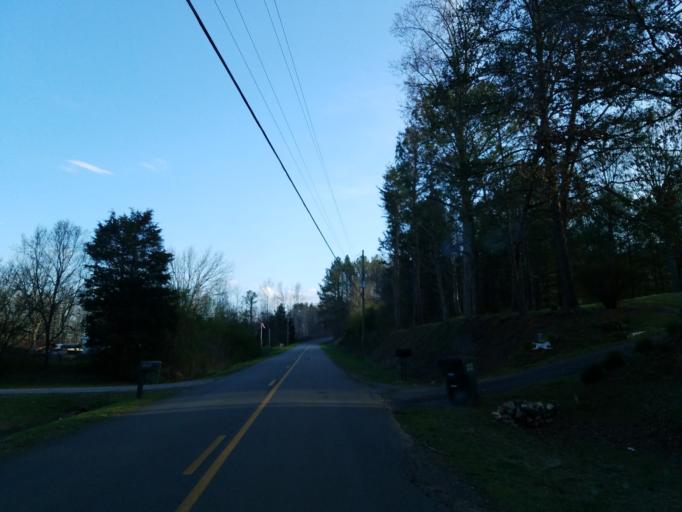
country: US
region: Georgia
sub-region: Pickens County
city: Jasper
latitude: 34.5013
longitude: -84.6005
